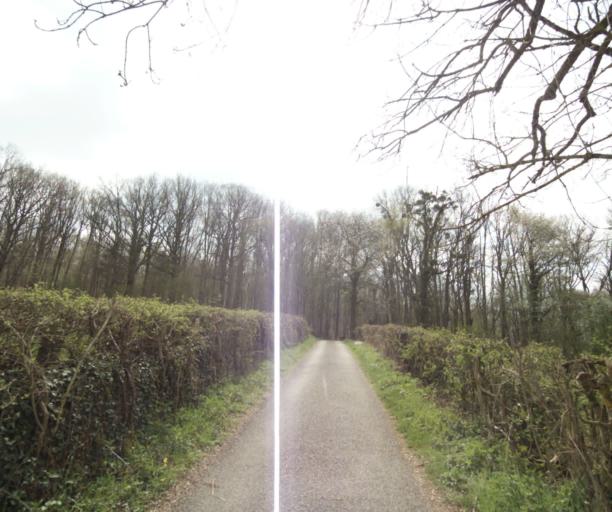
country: FR
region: Bourgogne
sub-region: Departement de Saone-et-Loire
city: Charolles
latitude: 46.3904
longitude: 4.2717
